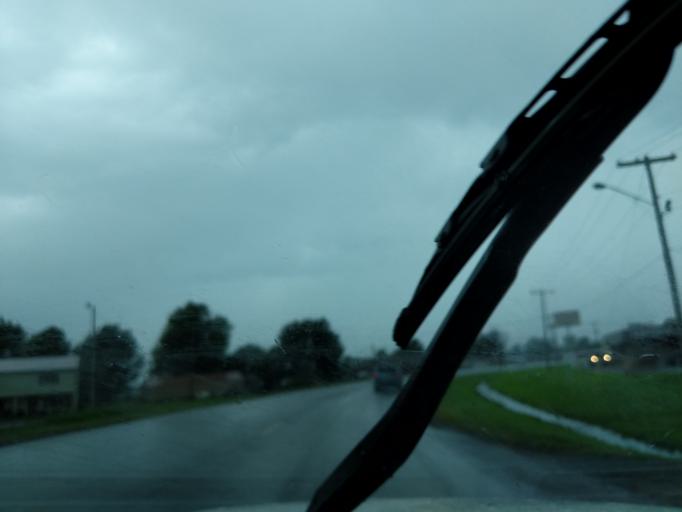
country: US
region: Missouri
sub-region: New Madrid County
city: New Madrid
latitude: 36.5959
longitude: -89.5328
